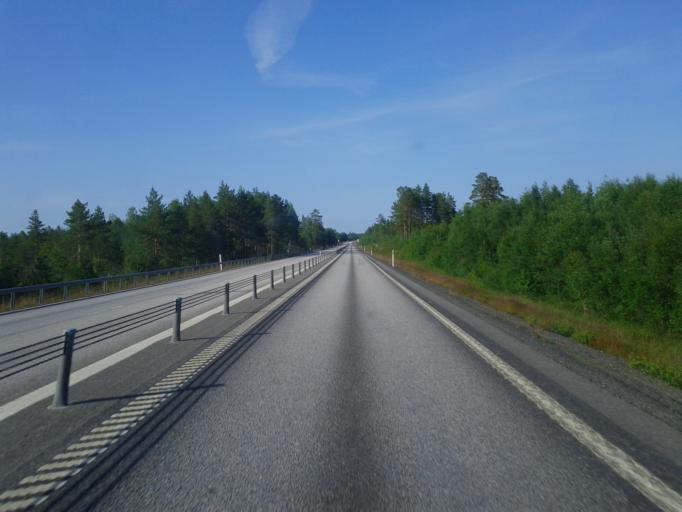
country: SE
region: Vaesterbotten
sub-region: Umea Kommun
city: Saevar
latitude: 63.9424
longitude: 20.6535
